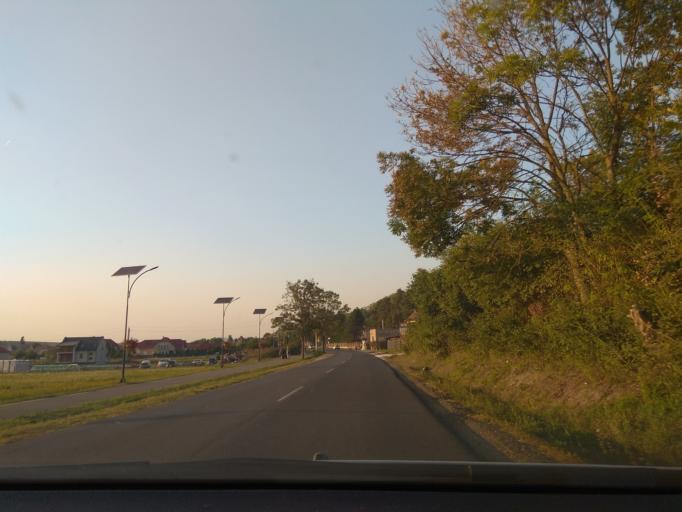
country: HU
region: Heves
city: Egerszalok
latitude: 47.8621
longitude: 20.3281
